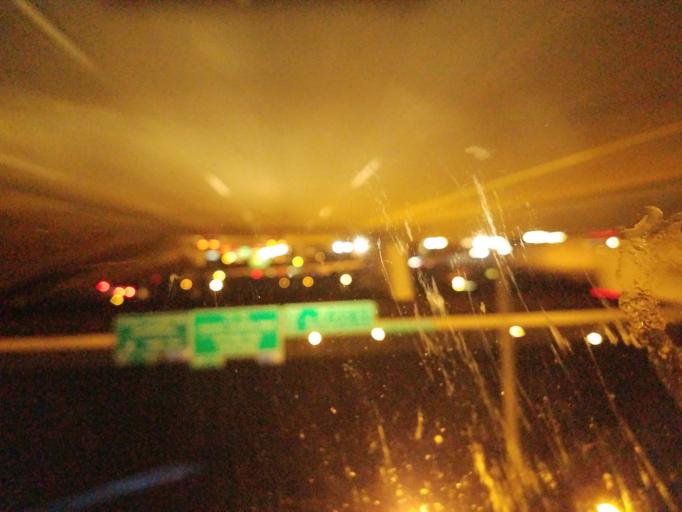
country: US
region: Iowa
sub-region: Polk County
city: Des Moines
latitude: 41.5958
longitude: -93.6450
